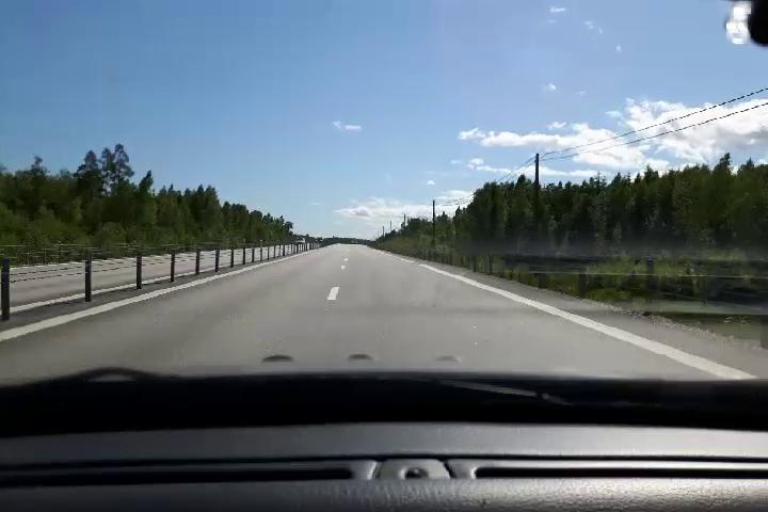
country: SE
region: Gaevleborg
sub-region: Hudiksvalls Kommun
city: Iggesund
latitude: 61.6784
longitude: 17.0361
